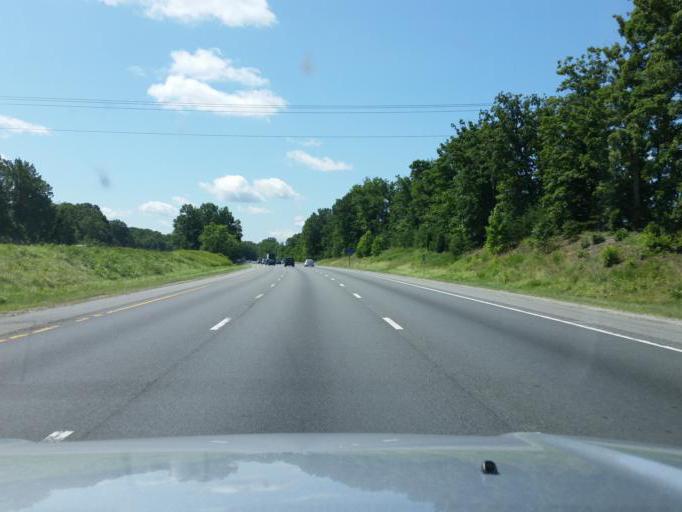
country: US
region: Virginia
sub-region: Spotsylvania County
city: Spotsylvania Courthouse
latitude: 38.2192
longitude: -77.5000
